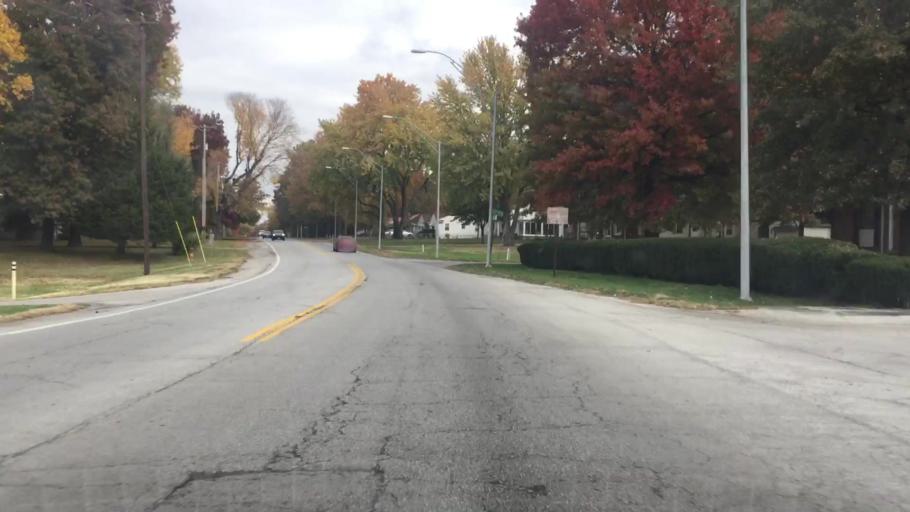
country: US
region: Missouri
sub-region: Jackson County
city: Raytown
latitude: 39.0303
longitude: -94.4392
